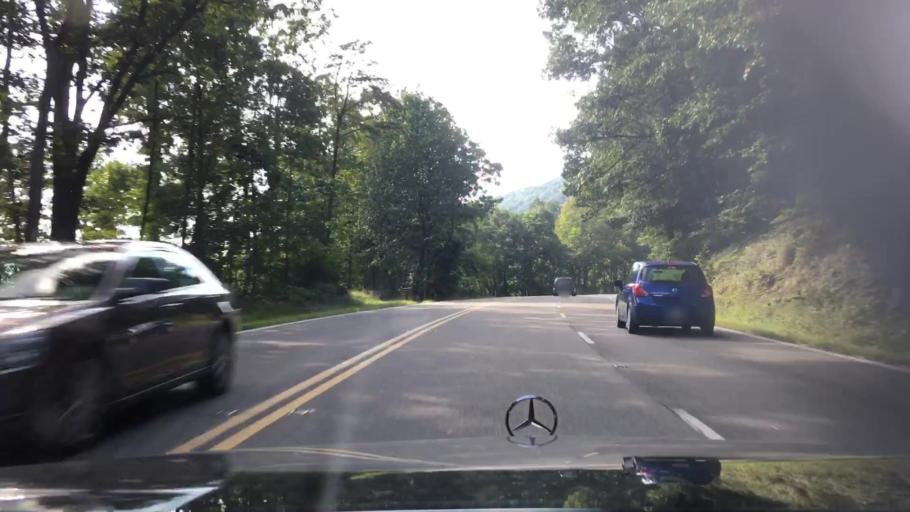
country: US
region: Virginia
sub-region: City of Waynesboro
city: Waynesboro
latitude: 38.0375
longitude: -78.8222
